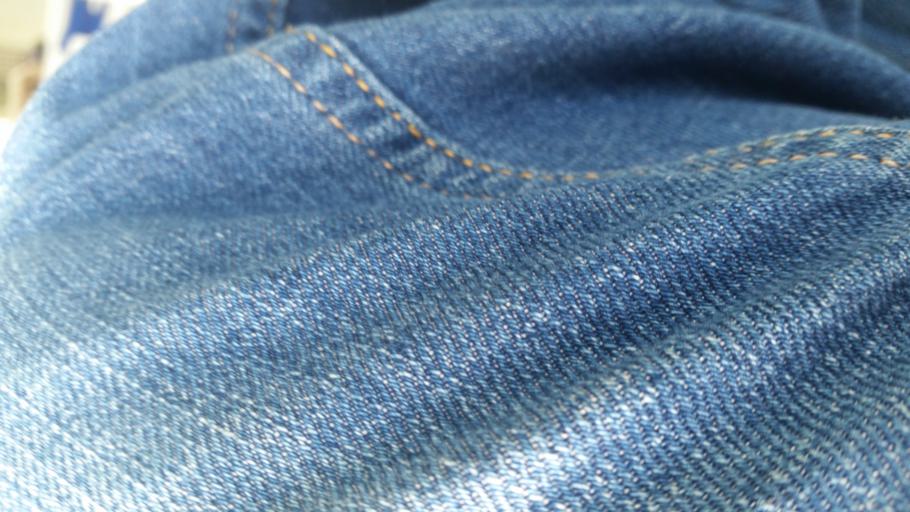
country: TR
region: Antalya
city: Belek
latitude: 36.8429
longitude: 31.0874
